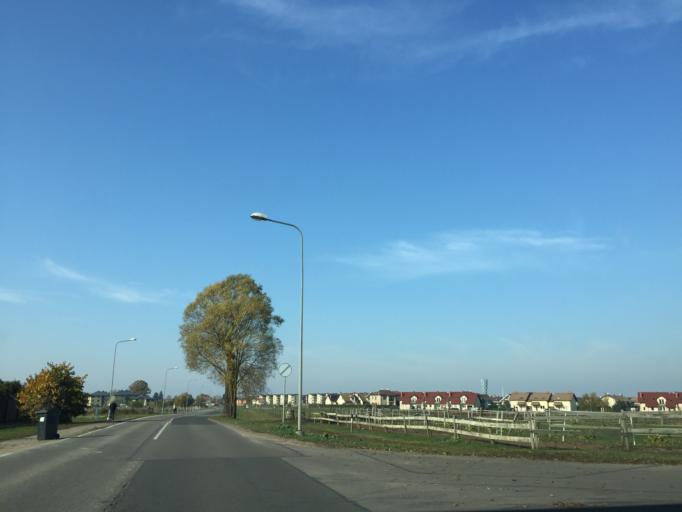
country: LV
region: Marupe
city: Marupe
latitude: 56.8883
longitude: 24.0621
